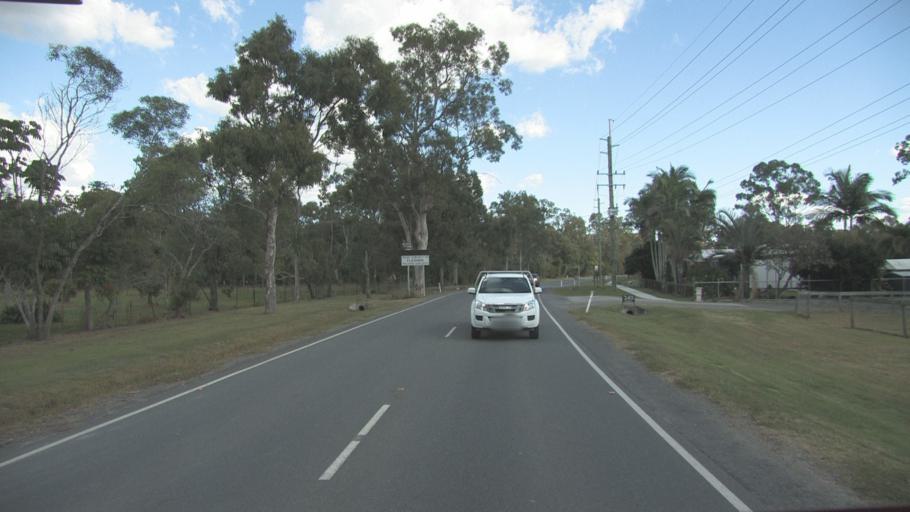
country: AU
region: Queensland
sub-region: Logan
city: Beenleigh
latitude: -27.6614
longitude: 153.2167
